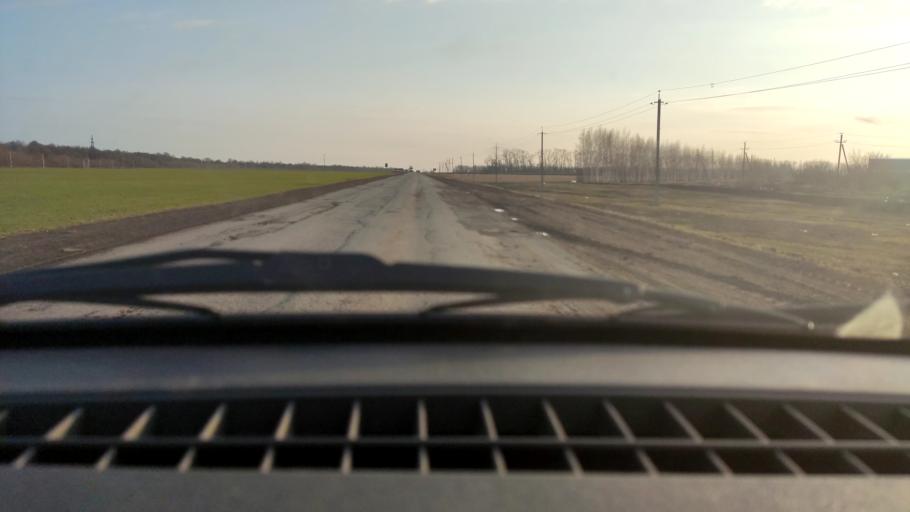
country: RU
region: Bashkortostan
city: Chishmy
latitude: 54.5672
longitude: 55.3501
